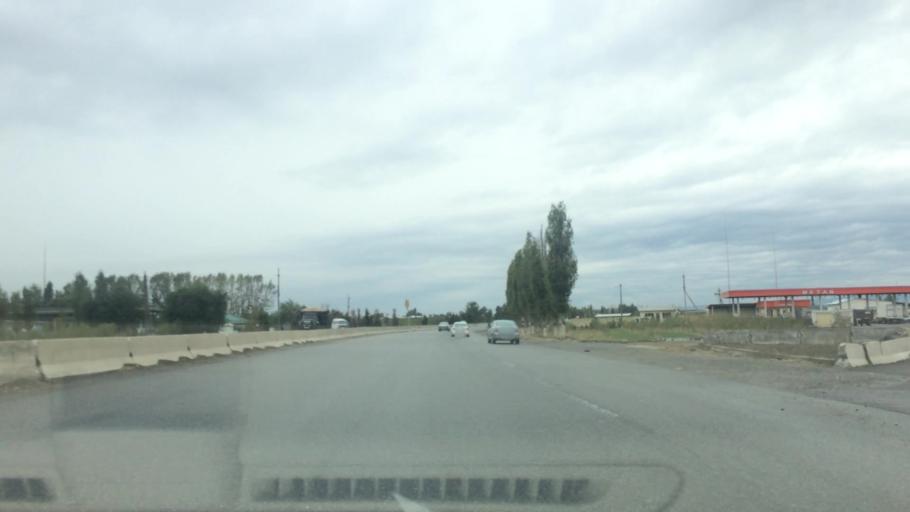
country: UZ
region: Jizzax
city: Jizzax
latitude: 40.0230
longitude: 67.6151
